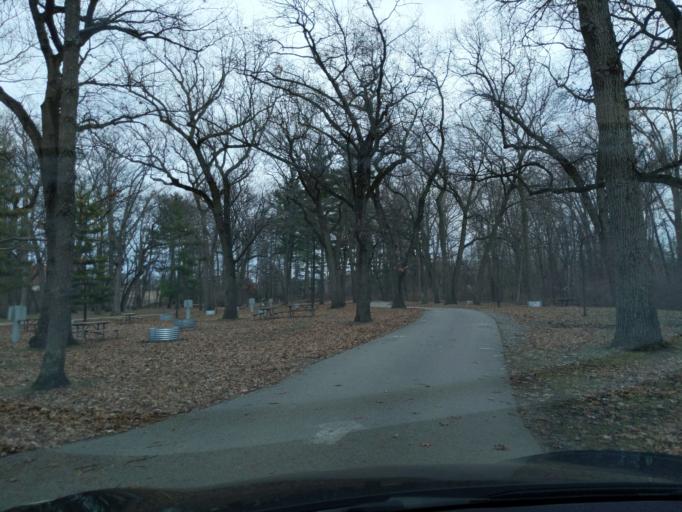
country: US
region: Michigan
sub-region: Bay County
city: Bay City
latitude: 43.6630
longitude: -83.8996
